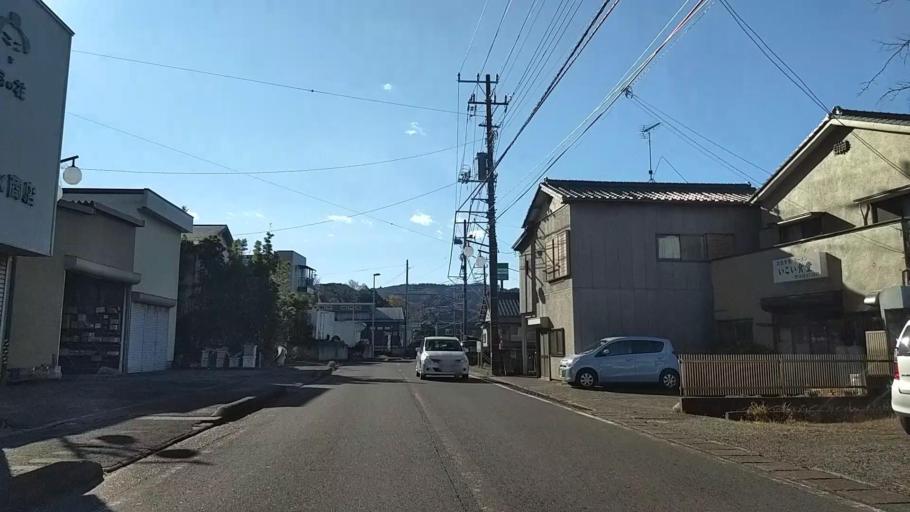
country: JP
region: Chiba
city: Futtsu
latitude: 35.2207
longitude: 139.8725
